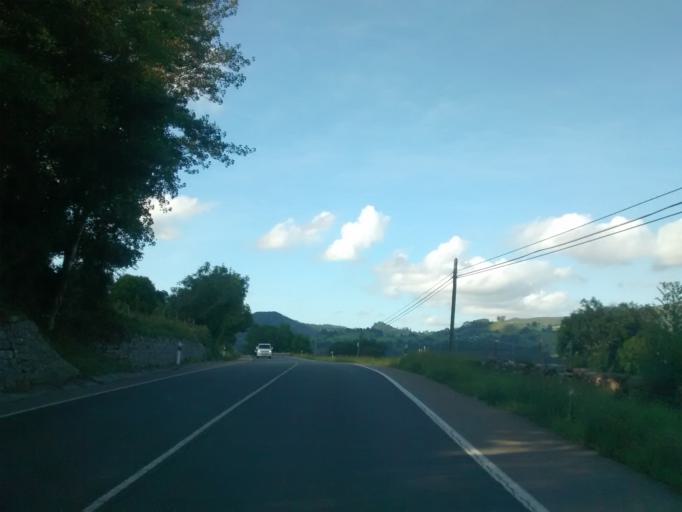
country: ES
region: Cantabria
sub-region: Provincia de Cantabria
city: Corvera
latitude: 43.2585
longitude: -3.9480
